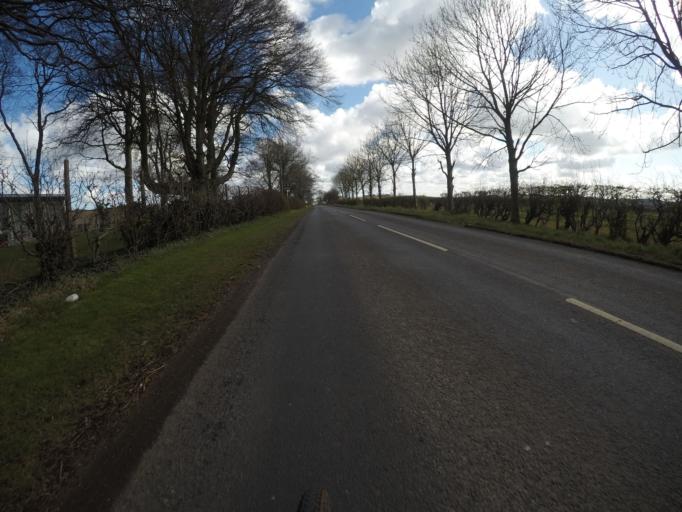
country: GB
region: Scotland
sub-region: North Ayrshire
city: Dreghorn
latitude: 55.5948
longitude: -4.6133
